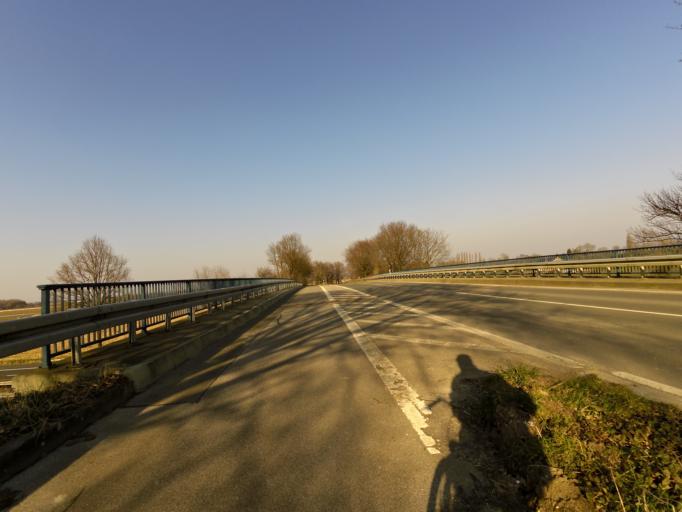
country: NL
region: Gelderland
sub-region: Gemeente Montferland
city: s-Heerenberg
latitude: 51.8499
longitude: 6.2943
